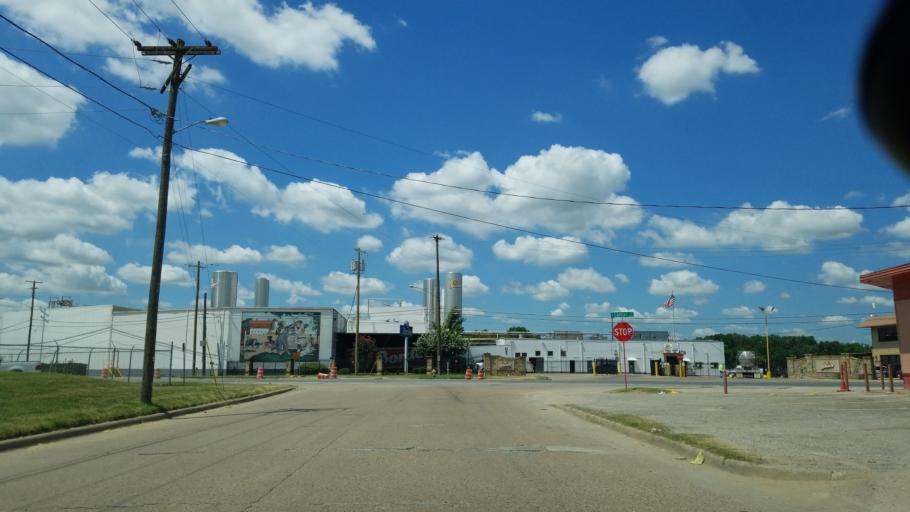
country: US
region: Texas
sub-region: Dallas County
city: Dallas
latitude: 32.7431
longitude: -96.7584
